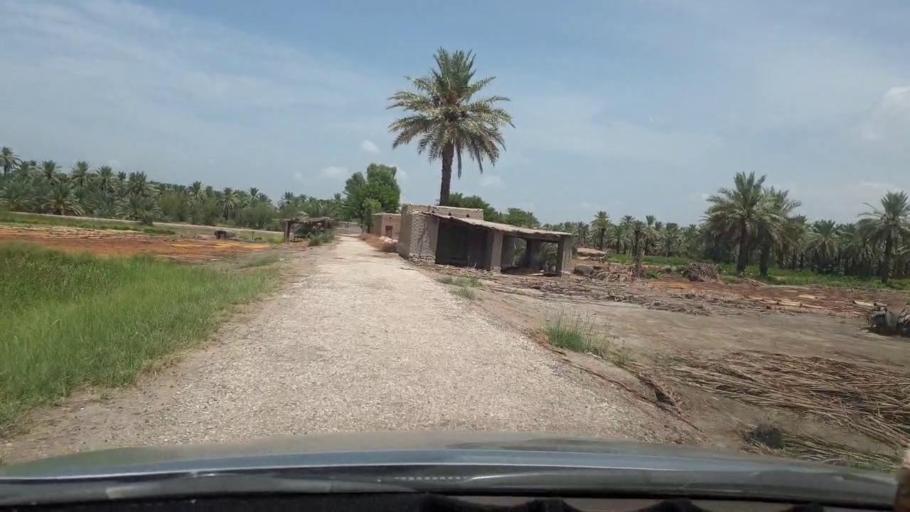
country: PK
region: Sindh
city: Khairpur
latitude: 27.4444
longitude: 68.7766
